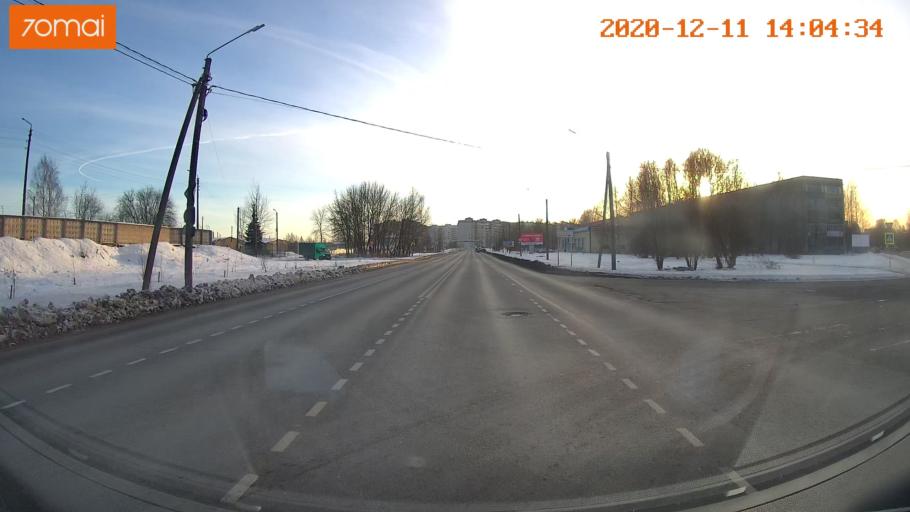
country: RU
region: Kostroma
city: Oktyabr'skiy
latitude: 57.7541
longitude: 41.0164
